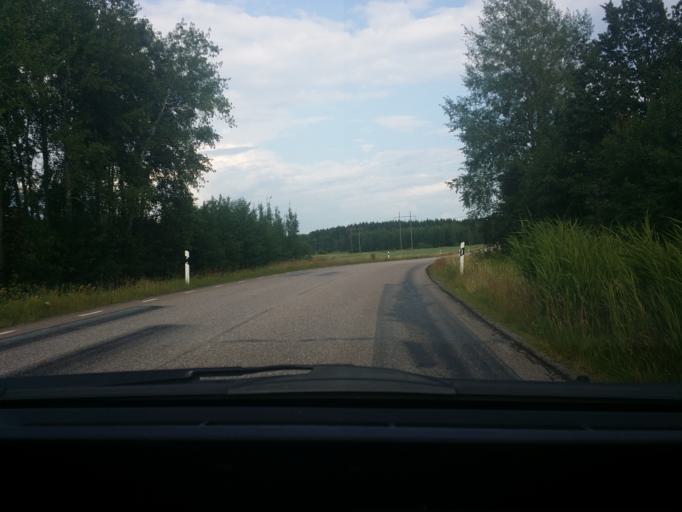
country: SE
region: Vaestmanland
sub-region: Hallstahammars Kommun
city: Kolback
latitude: 59.5638
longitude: 16.2688
